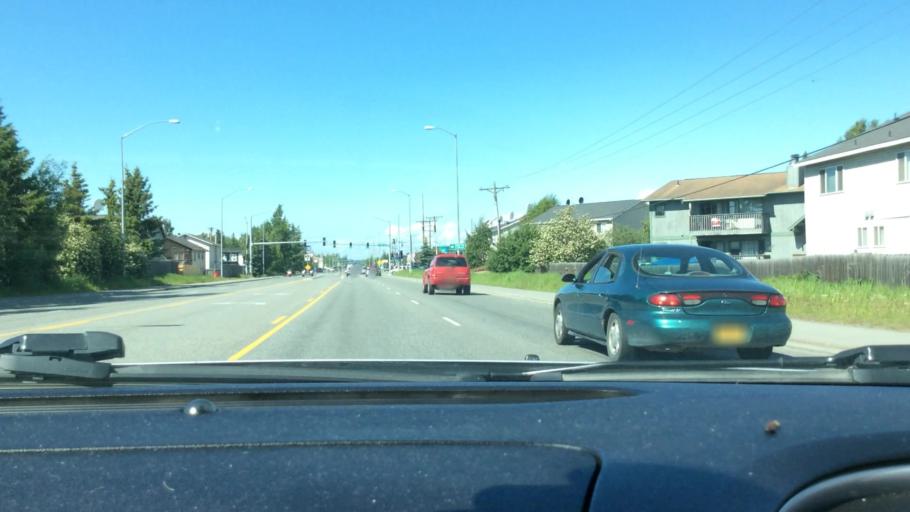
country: US
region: Alaska
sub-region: Anchorage Municipality
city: Anchorage
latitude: 61.2170
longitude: -149.7784
